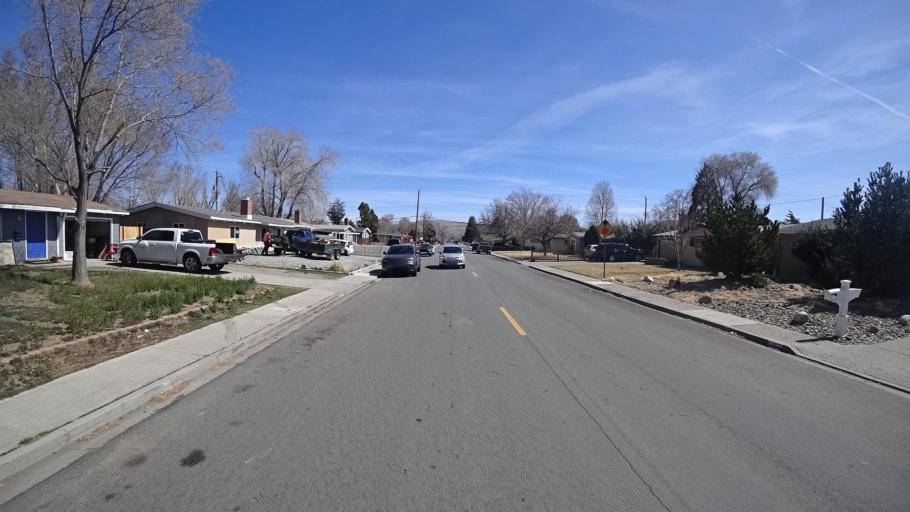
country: US
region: Nevada
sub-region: Washoe County
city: Sparks
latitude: 39.5474
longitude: -119.7586
